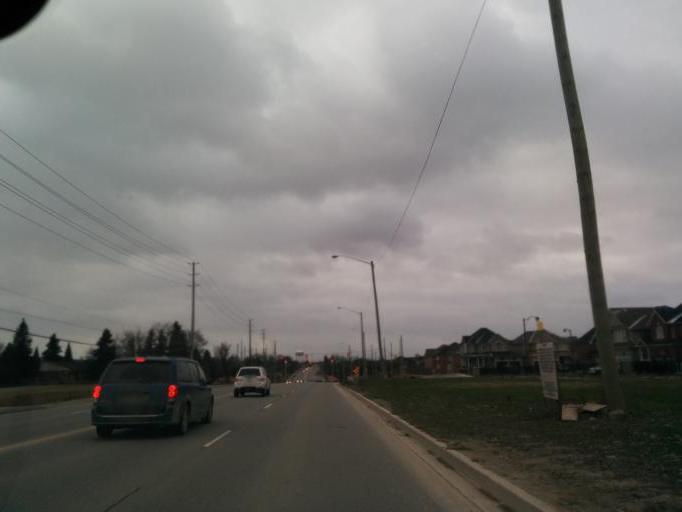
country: CA
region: Ontario
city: Brampton
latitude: 43.7423
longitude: -79.8161
